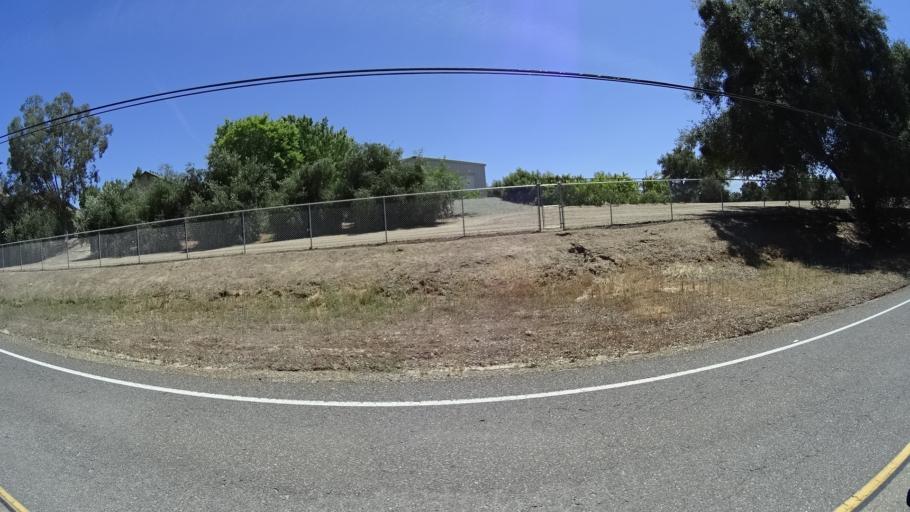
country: US
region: California
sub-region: Calaveras County
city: Valley Springs
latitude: 38.1934
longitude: -120.8900
